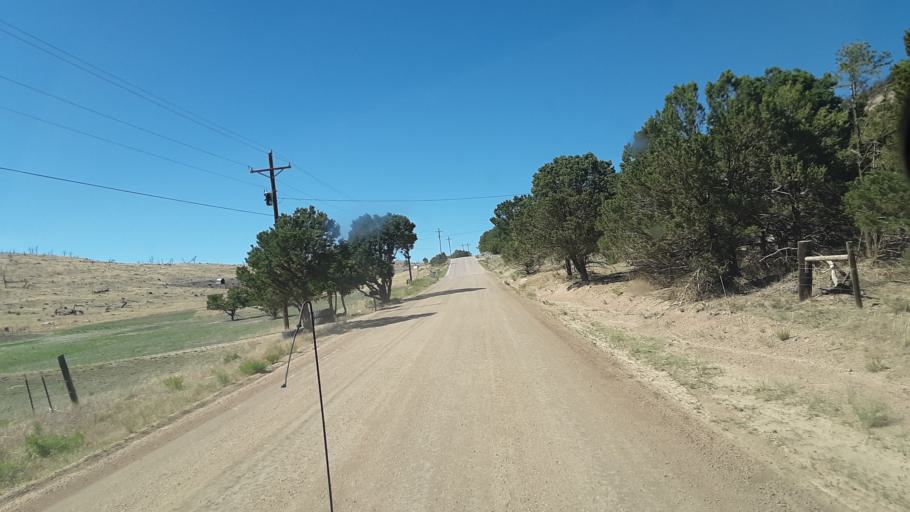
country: US
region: Colorado
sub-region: Custer County
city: Westcliffe
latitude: 38.3202
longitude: -105.4873
